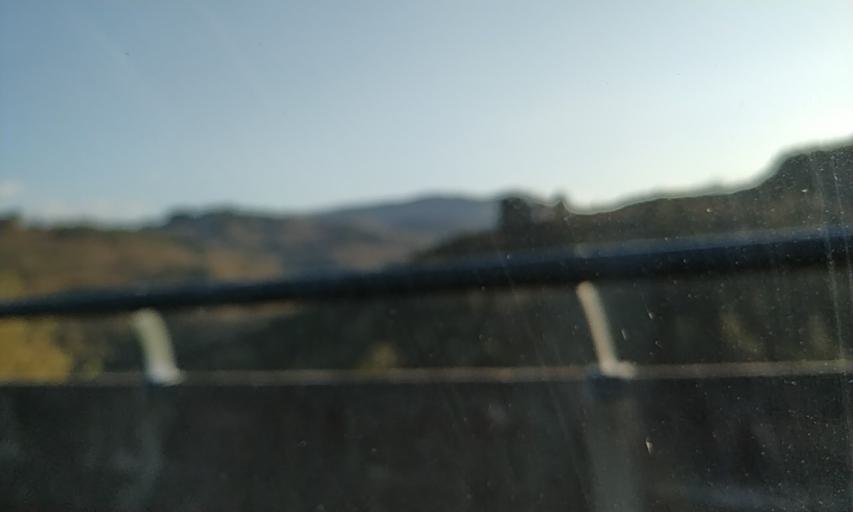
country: ES
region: Galicia
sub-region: Provincia de Lugo
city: Becerrea
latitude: 42.8596
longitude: -7.1308
